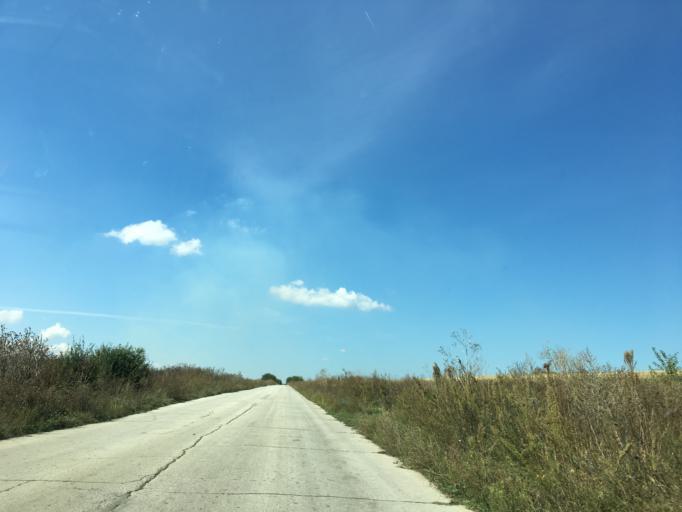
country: RO
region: Olt
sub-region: Comuna Orlea
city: Orlea
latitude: 43.6388
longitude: 24.3884
